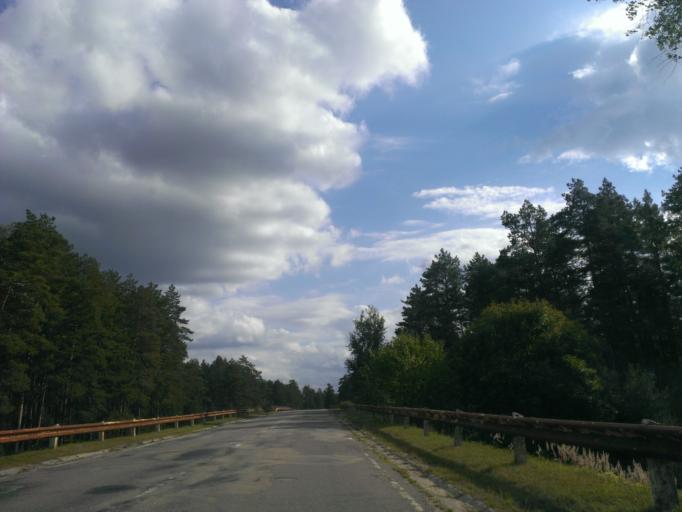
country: LV
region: Incukalns
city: Vangazi
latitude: 57.0818
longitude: 24.5203
